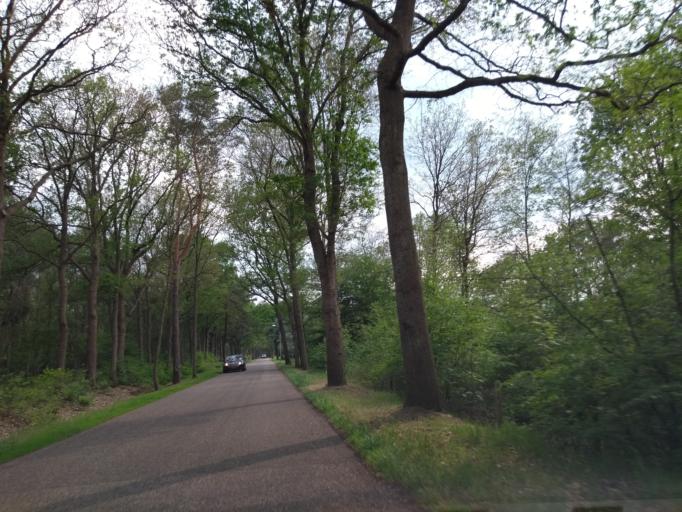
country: NL
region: Overijssel
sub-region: Gemeente Staphorst
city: Staphorst
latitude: 52.6430
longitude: 6.2848
